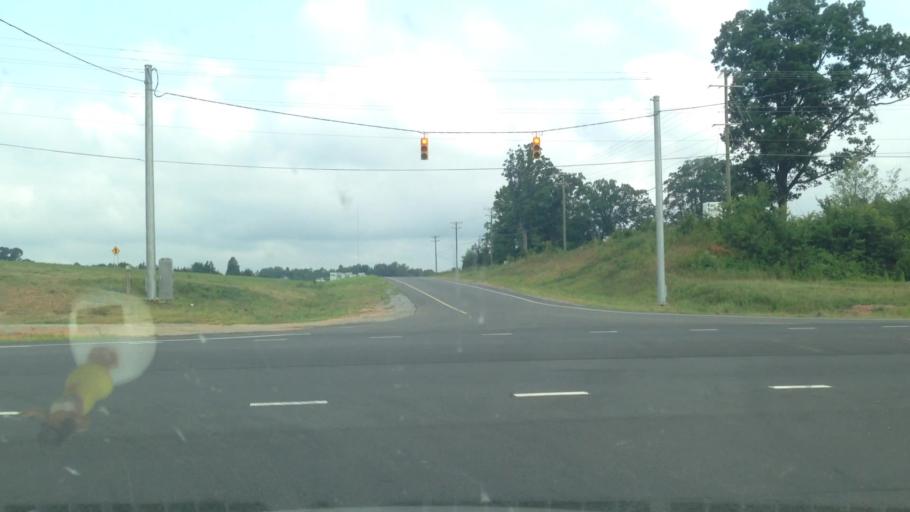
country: US
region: North Carolina
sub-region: Guilford County
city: Summerfield
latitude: 36.2472
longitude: -79.9196
